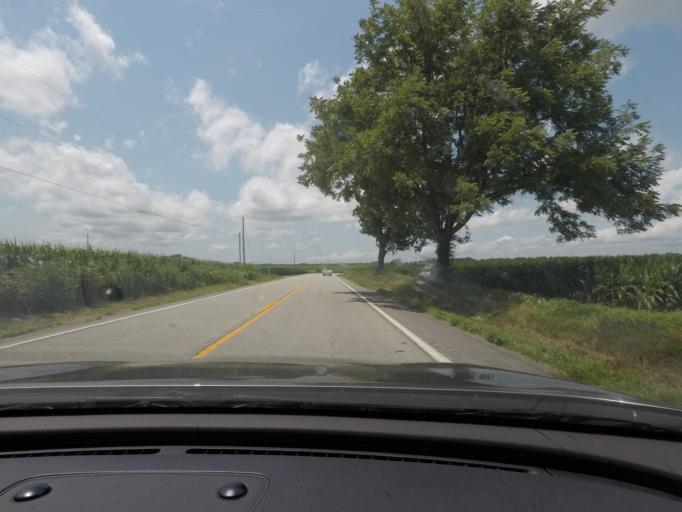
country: US
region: Missouri
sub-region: Carroll County
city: Carrollton
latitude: 39.1961
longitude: -93.4253
